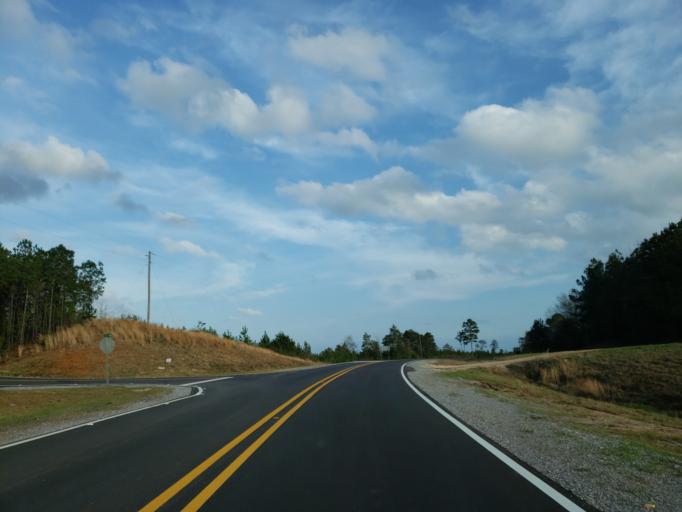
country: US
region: Mississippi
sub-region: Clarke County
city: Stonewall
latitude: 32.1806
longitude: -88.7078
